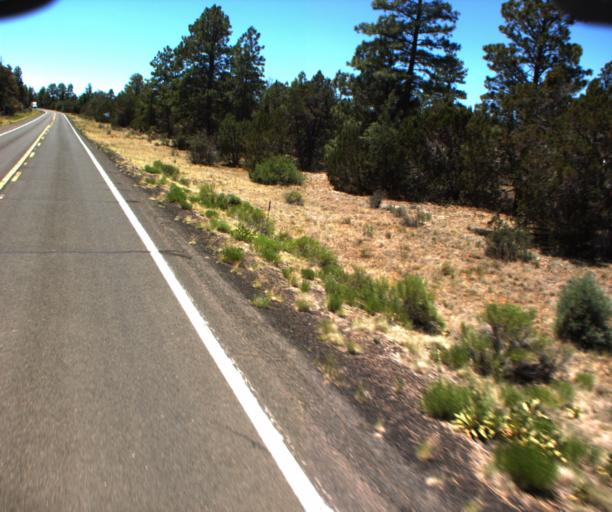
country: US
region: Arizona
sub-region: Gila County
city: Star Valley
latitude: 34.6886
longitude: -111.1116
